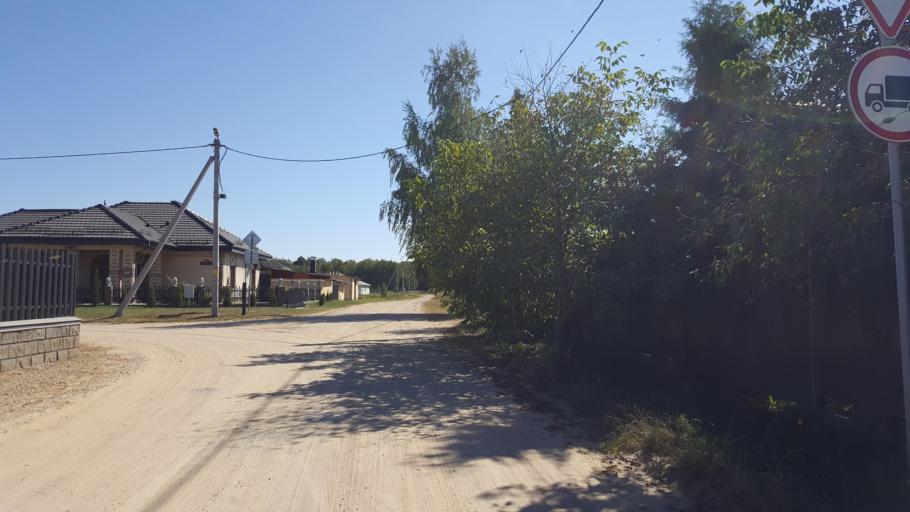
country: BY
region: Brest
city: Vysokaye
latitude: 52.2509
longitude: 23.4988
